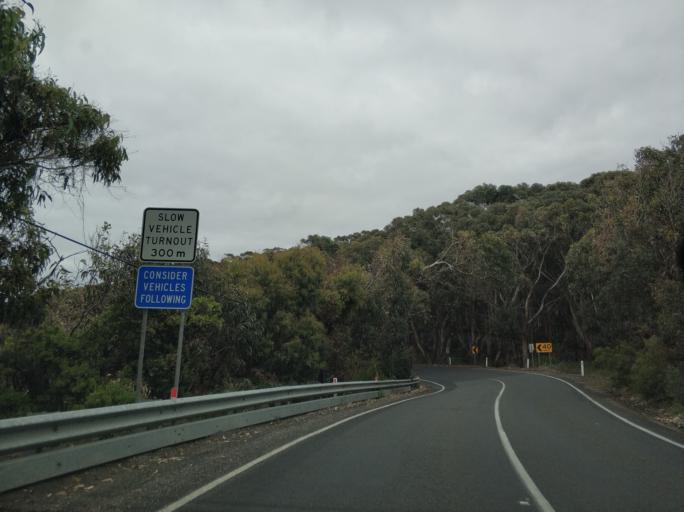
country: AU
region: Victoria
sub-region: Surf Coast
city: Anglesea
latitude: -38.4942
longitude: 144.0144
